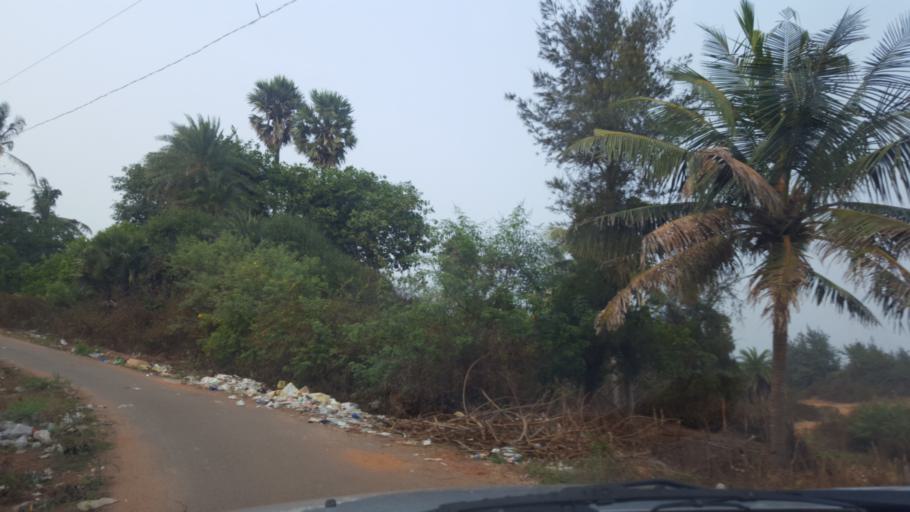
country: IN
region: Andhra Pradesh
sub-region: Srikakulam
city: Palasa
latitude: 18.7597
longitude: 84.5124
